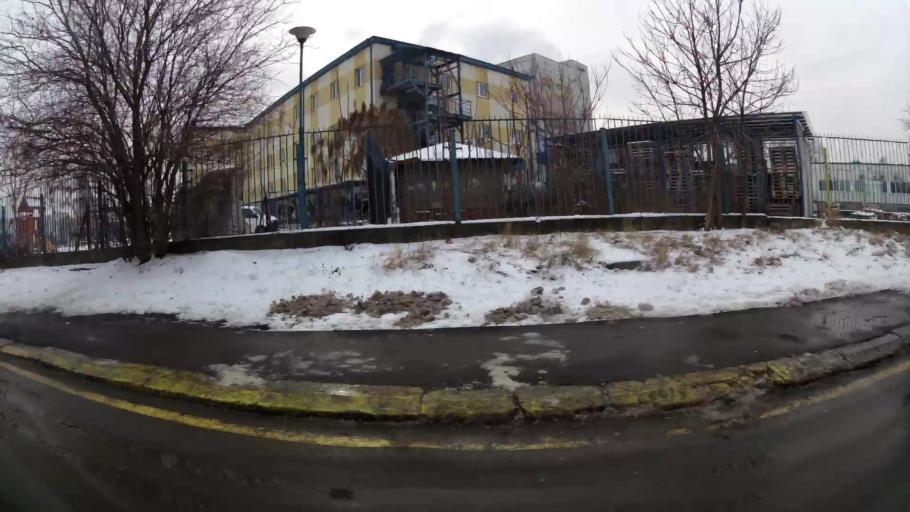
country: BG
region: Sofia-Capital
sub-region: Stolichna Obshtina
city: Sofia
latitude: 42.7069
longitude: 23.3394
